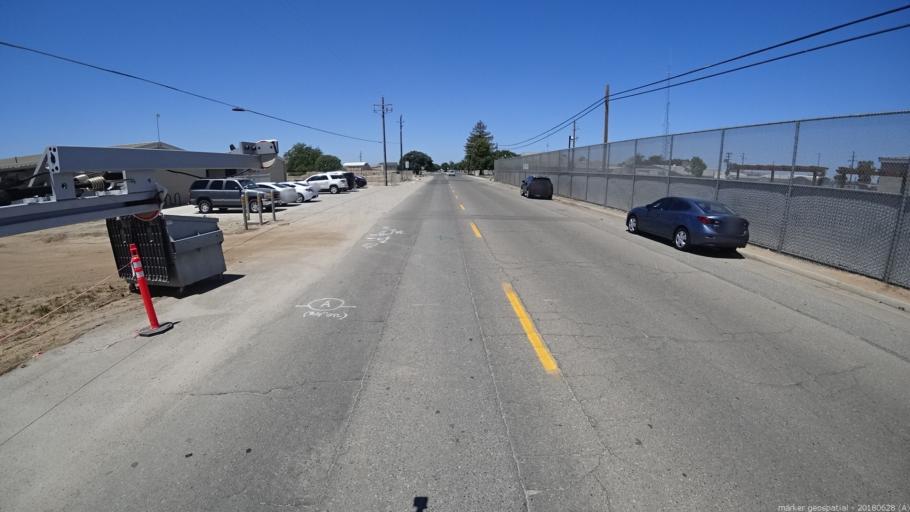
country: US
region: California
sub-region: Madera County
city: Parksdale
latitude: 36.9526
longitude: -120.0358
